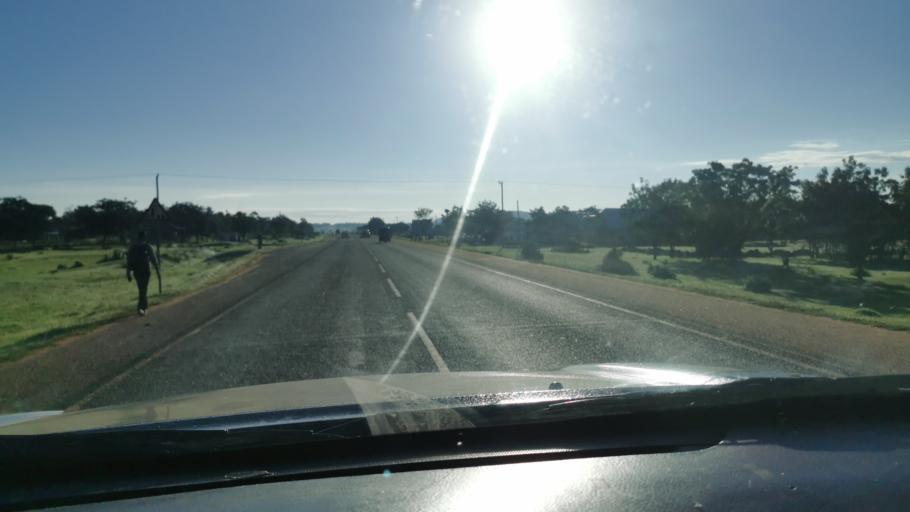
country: TZ
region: Shinyanga
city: Kahama
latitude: -3.8387
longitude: 32.6391
